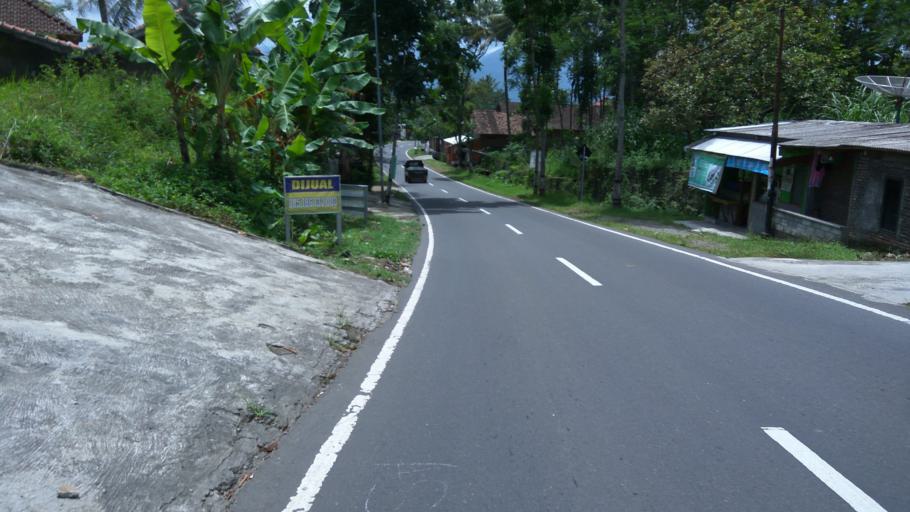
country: ID
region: Central Java
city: Ambarawa
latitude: -7.2464
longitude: 110.3985
